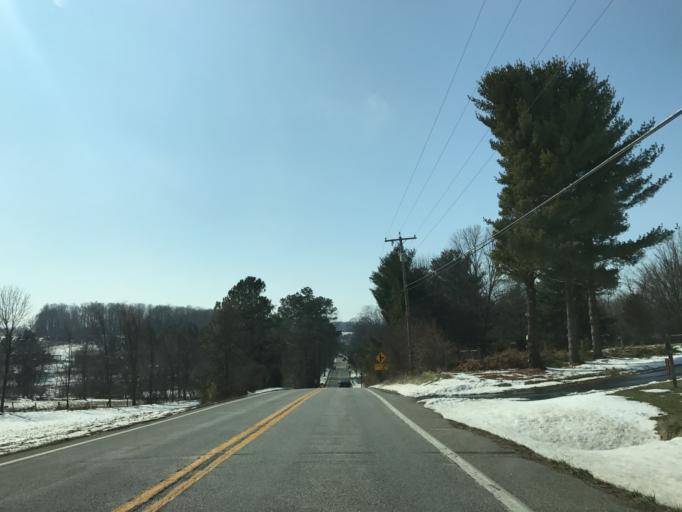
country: US
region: Pennsylvania
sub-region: York County
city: Stewartstown
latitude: 39.7040
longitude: -76.5101
